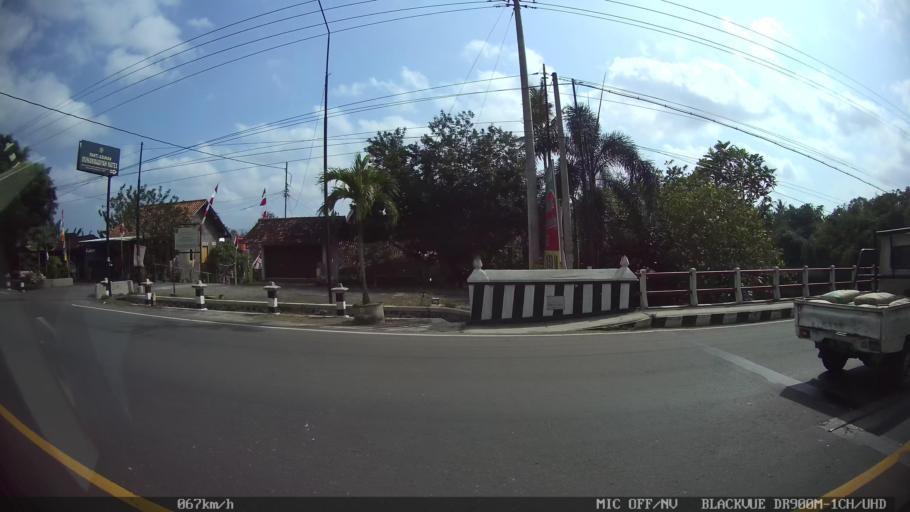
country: ID
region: Daerah Istimewa Yogyakarta
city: Srandakan
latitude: -7.8668
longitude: 110.1631
